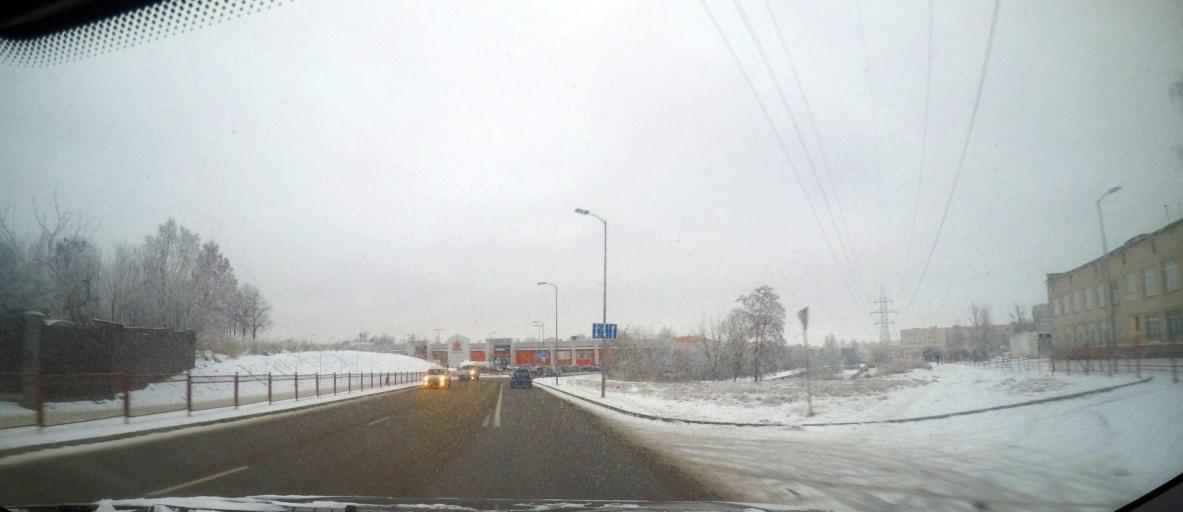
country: BY
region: Grodnenskaya
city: Hrodna
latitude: 53.6612
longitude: 23.8350
